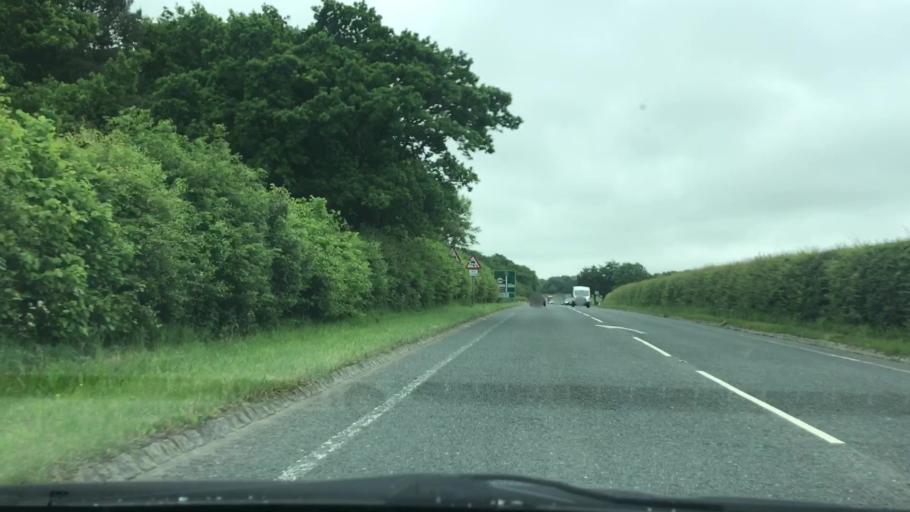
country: GB
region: England
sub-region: North Yorkshire
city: Pannal
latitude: 53.9626
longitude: -1.5009
